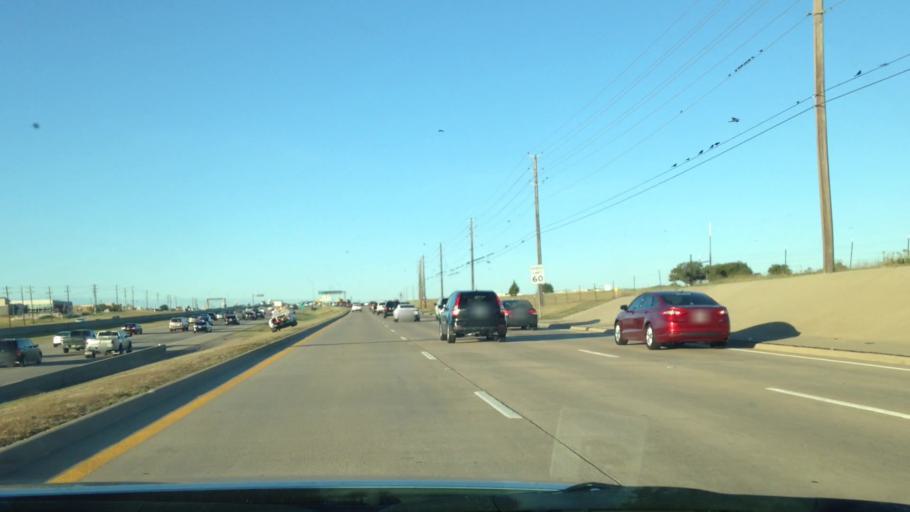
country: US
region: Texas
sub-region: Collin County
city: Frisco
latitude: 33.1164
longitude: -96.7590
